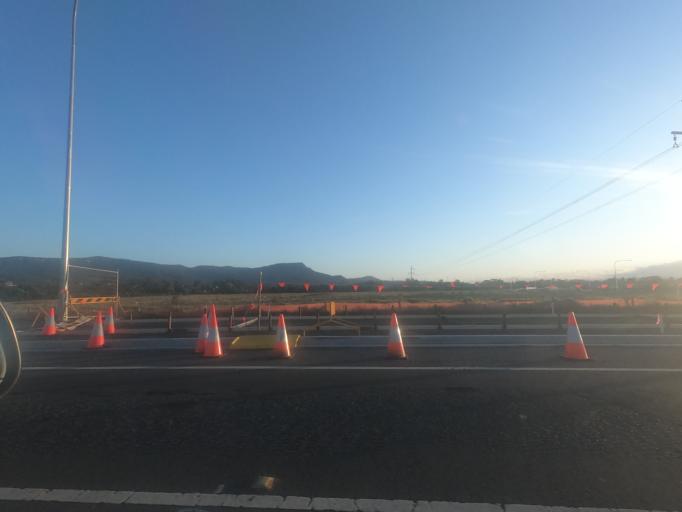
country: AU
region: New South Wales
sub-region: Wollongong
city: Dapto
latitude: -34.4986
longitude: 150.7799
